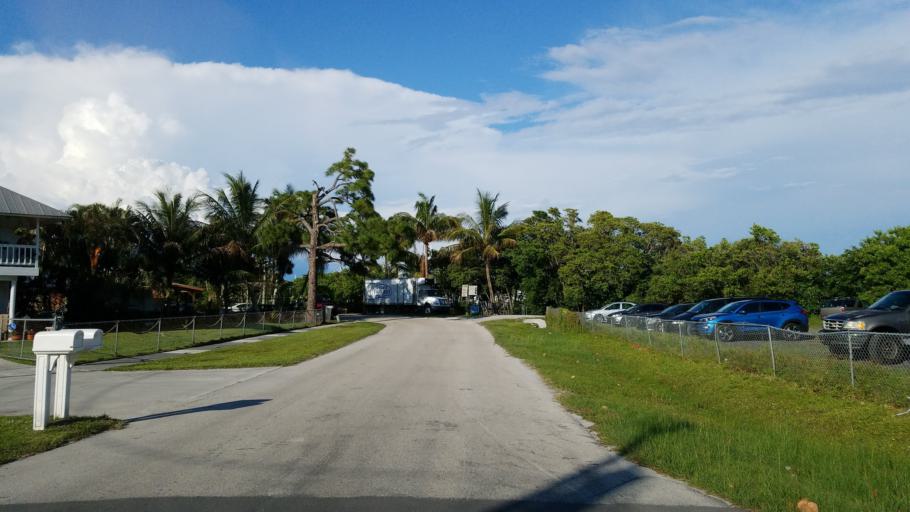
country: US
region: Florida
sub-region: Martin County
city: Port Salerno
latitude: 27.1476
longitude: -80.1968
